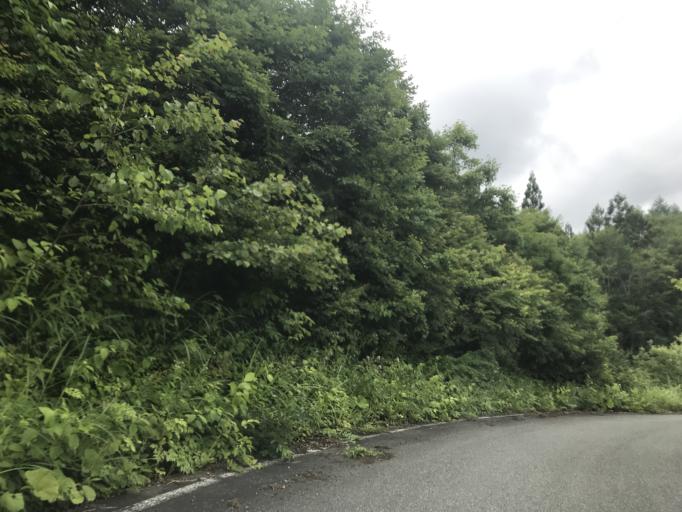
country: JP
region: Iwate
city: Ichinoseki
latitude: 38.9356
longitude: 140.8779
